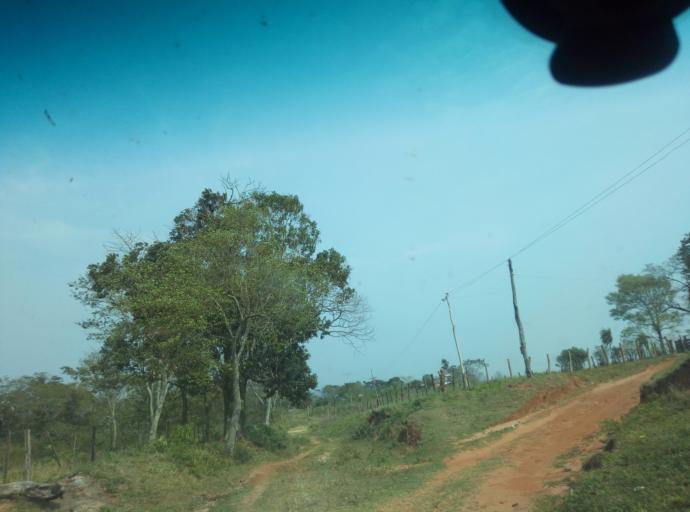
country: PY
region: Caaguazu
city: San Joaquin
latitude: -25.1428
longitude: -56.1025
